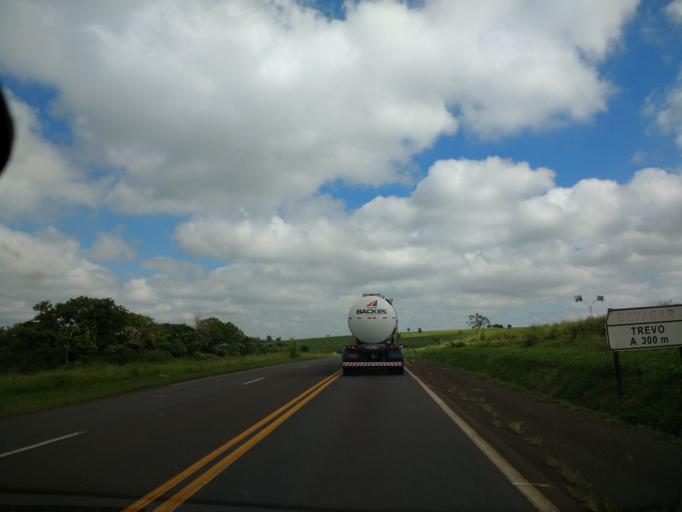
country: BR
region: Parana
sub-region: Cruzeiro Do Oeste
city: Cruzeiro do Oeste
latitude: -23.7726
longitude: -53.0170
